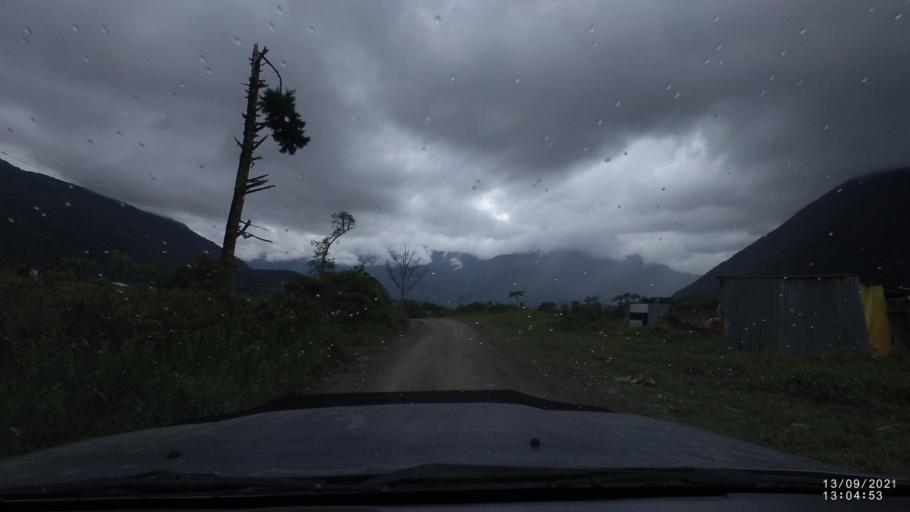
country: BO
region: Cochabamba
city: Colomi
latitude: -17.2237
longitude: -65.8209
